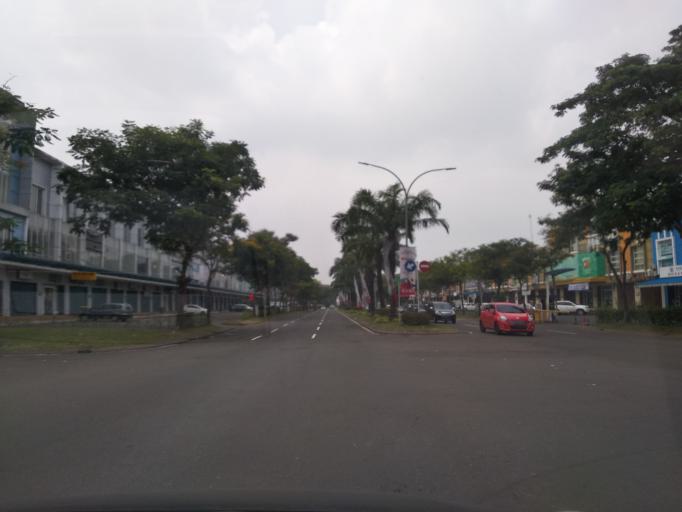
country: ID
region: West Java
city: Bekasi
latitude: -6.2891
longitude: 107.0437
